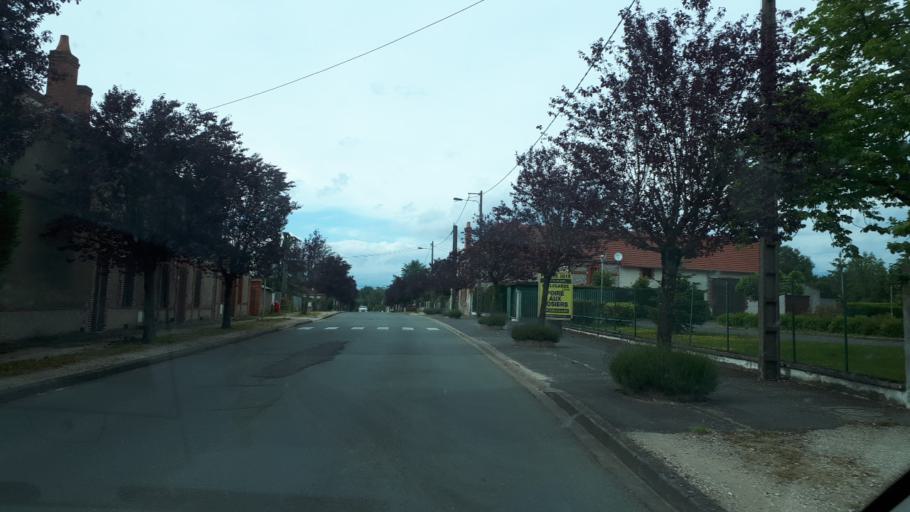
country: FR
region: Centre
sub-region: Departement du Loir-et-Cher
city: Villefranche-sur-Cher
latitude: 47.2960
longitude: 1.7699
